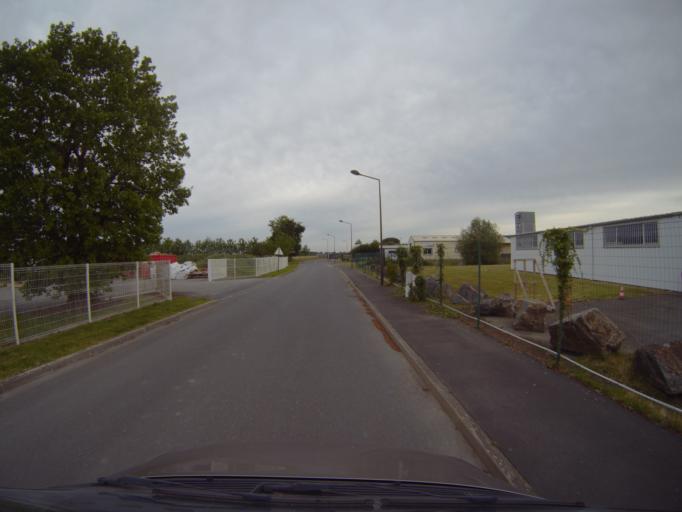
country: FR
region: Pays de la Loire
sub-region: Departement de la Loire-Atlantique
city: La Planche
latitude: 47.0196
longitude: -1.4261
